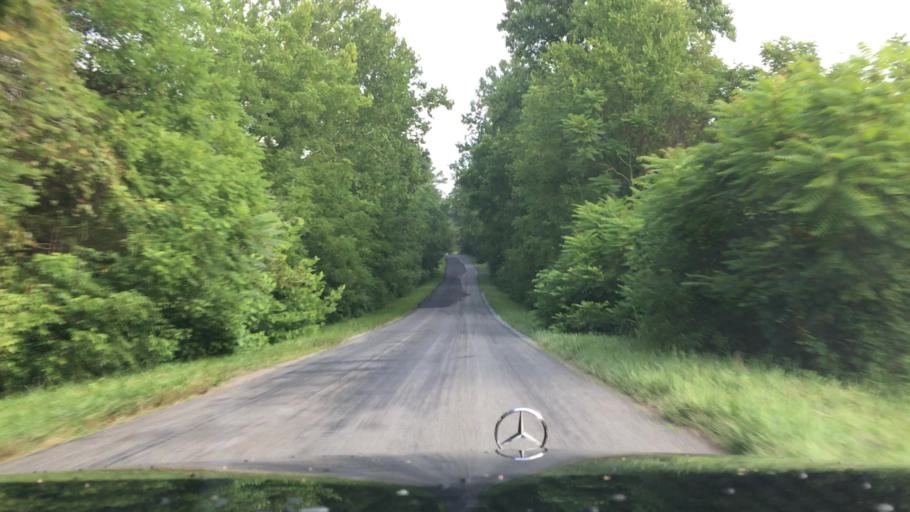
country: US
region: Virginia
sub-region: Campbell County
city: Timberlake
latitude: 37.2477
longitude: -79.3056
